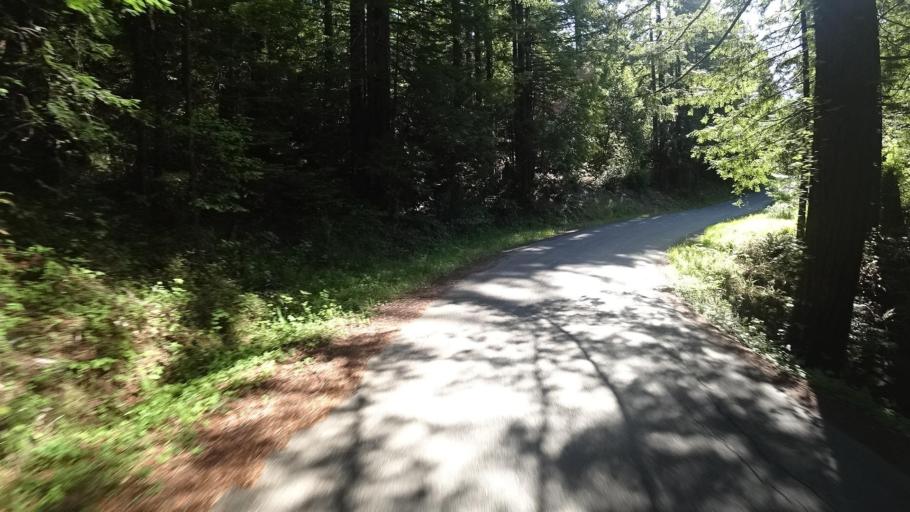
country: US
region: California
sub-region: Humboldt County
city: Rio Dell
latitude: 40.4575
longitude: -124.0194
